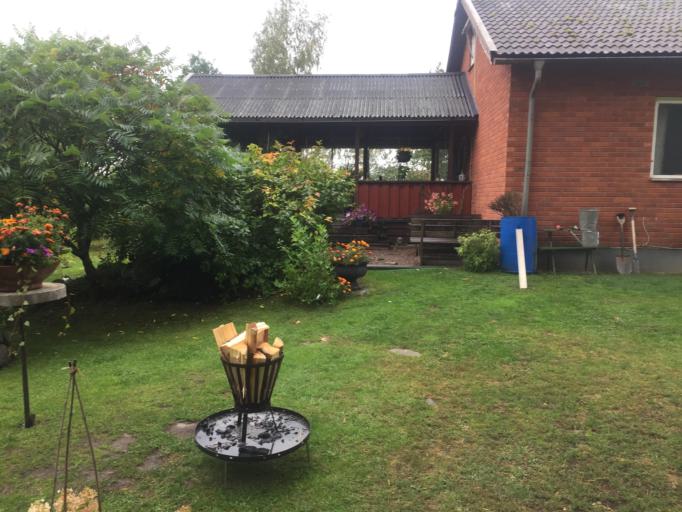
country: SE
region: Stockholm
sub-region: Sigtuna Kommun
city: Marsta
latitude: 59.7417
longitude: 17.9605
